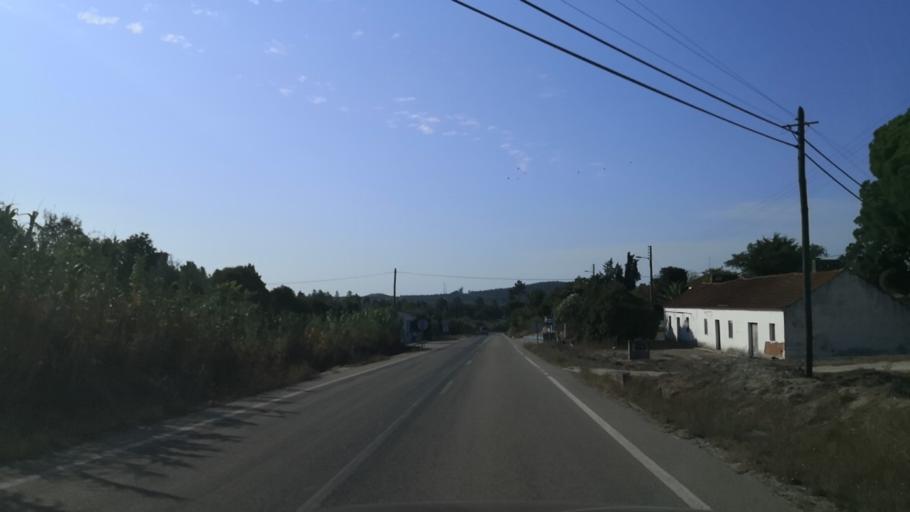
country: PT
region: Santarem
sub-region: Almeirim
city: Fazendas de Almeirim
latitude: 39.1035
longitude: -8.5773
